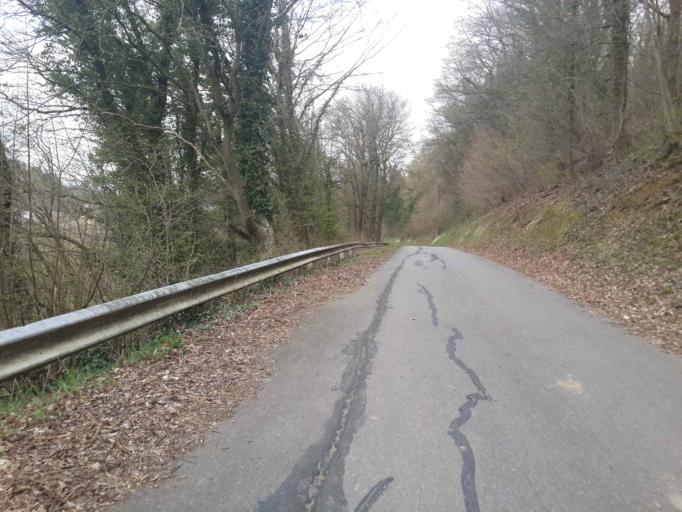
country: DE
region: Baden-Wuerttemberg
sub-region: Karlsruhe Region
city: Billigheim
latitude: 49.3521
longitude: 9.2598
